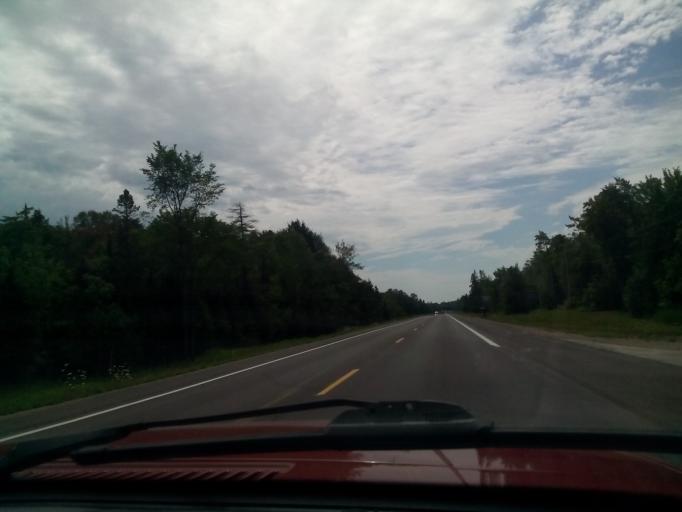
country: US
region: Michigan
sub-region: Schoolcraft County
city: Manistique
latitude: 46.0716
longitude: -85.9584
